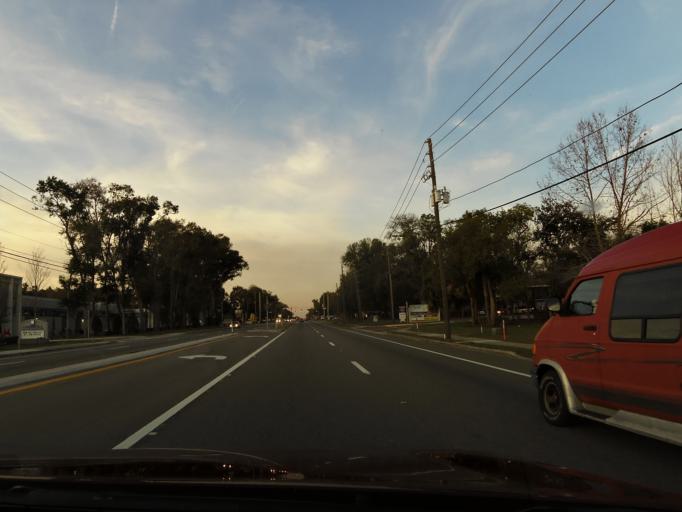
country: US
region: Florida
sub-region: Volusia County
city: North DeLand
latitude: 29.0585
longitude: -81.3044
